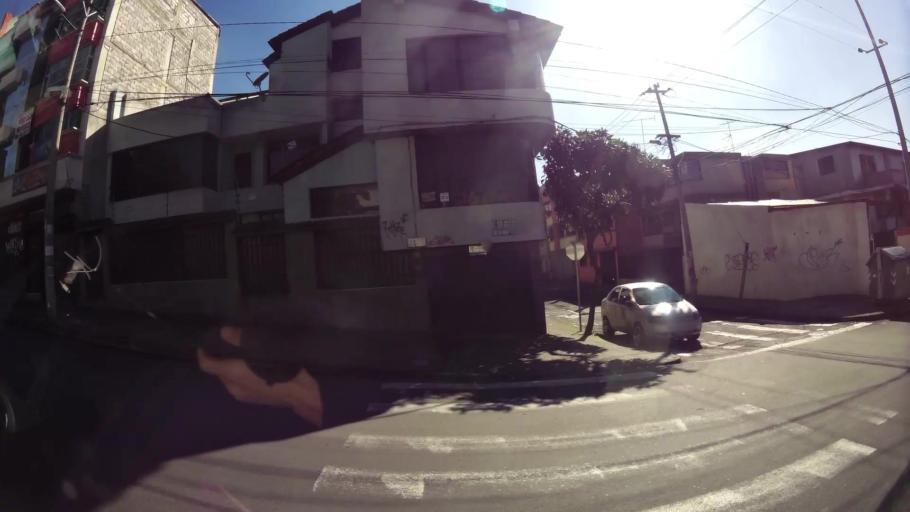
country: EC
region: Pichincha
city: Quito
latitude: -0.2501
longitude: -78.5347
